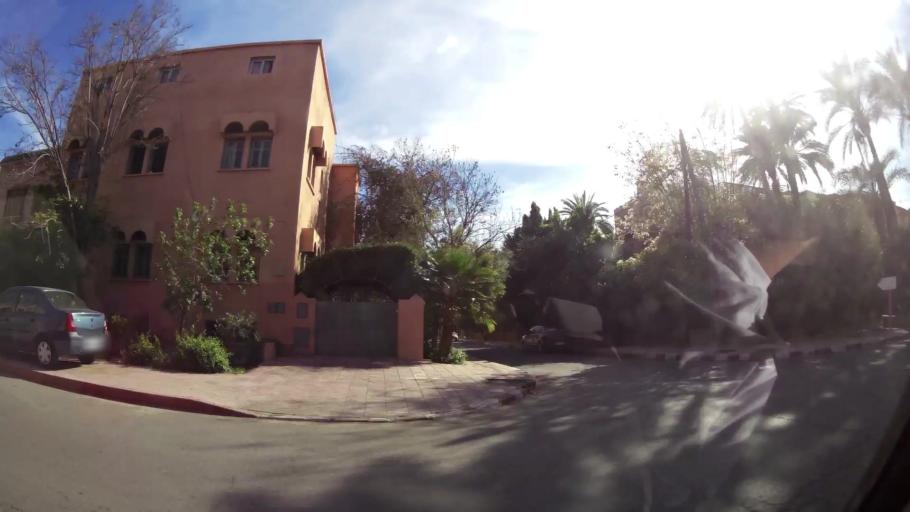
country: MA
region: Marrakech-Tensift-Al Haouz
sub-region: Marrakech
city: Marrakesh
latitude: 31.6570
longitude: -8.0145
